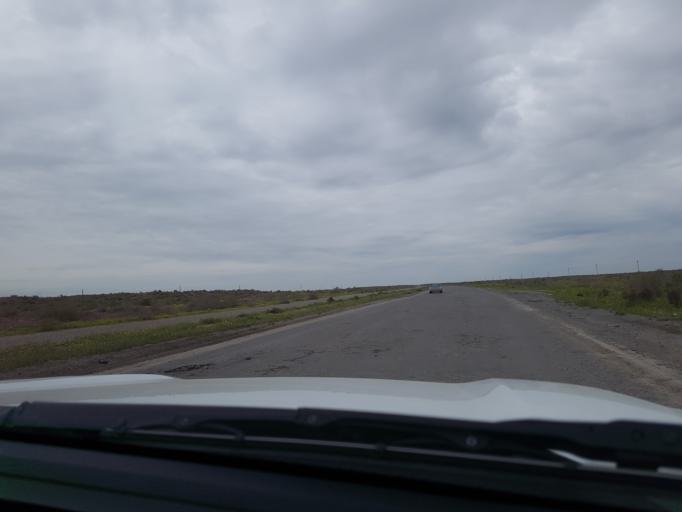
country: TM
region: Mary
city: Bayramaly
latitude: 37.9341
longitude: 62.6277
